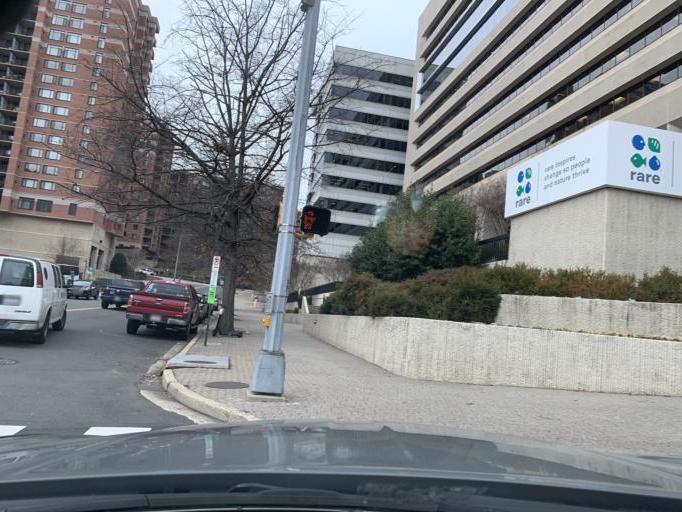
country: US
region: Virginia
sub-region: Arlington County
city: Arlington
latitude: 38.8883
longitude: -77.0835
